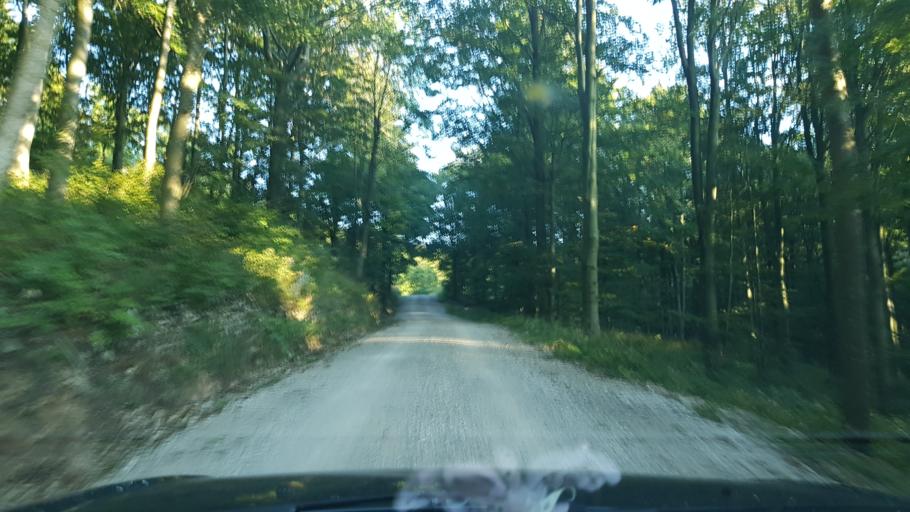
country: SI
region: Vipava
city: Vipava
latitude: 45.7804
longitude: 14.0433
